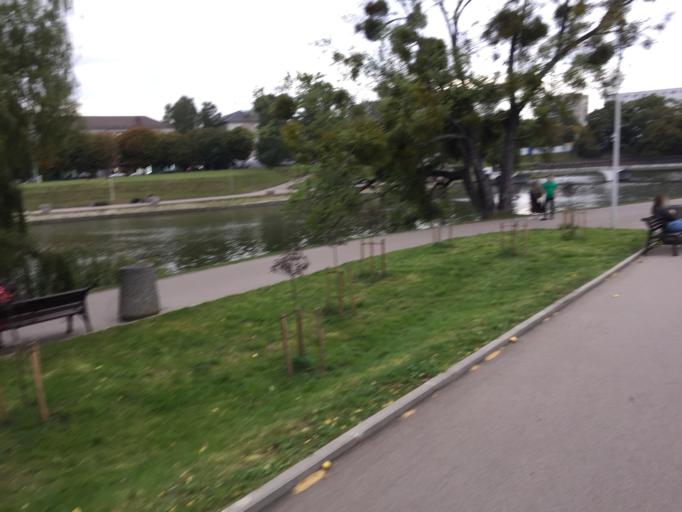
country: RU
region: Kaliningrad
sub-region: Gorod Kaliningrad
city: Kaliningrad
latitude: 54.7124
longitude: 20.5153
